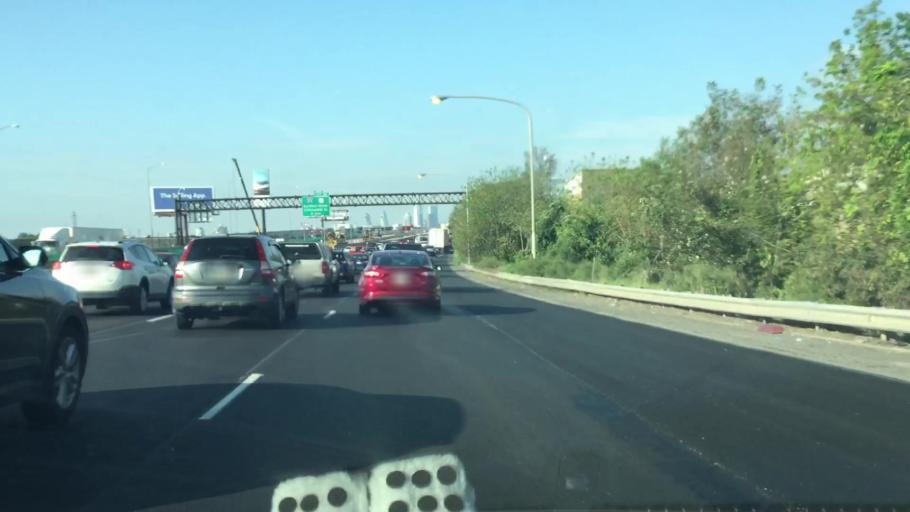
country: US
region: New Jersey
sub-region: Camden County
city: Merchantville
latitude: 39.9810
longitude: -75.1044
